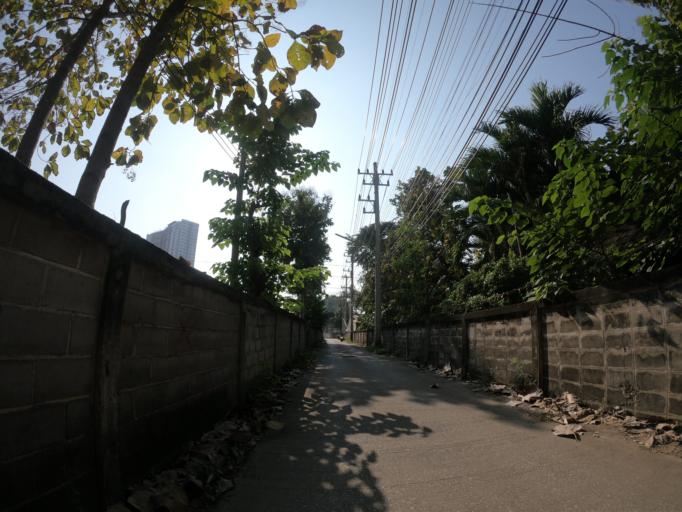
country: TH
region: Chiang Mai
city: Chiang Mai
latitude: 18.8027
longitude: 99.0155
